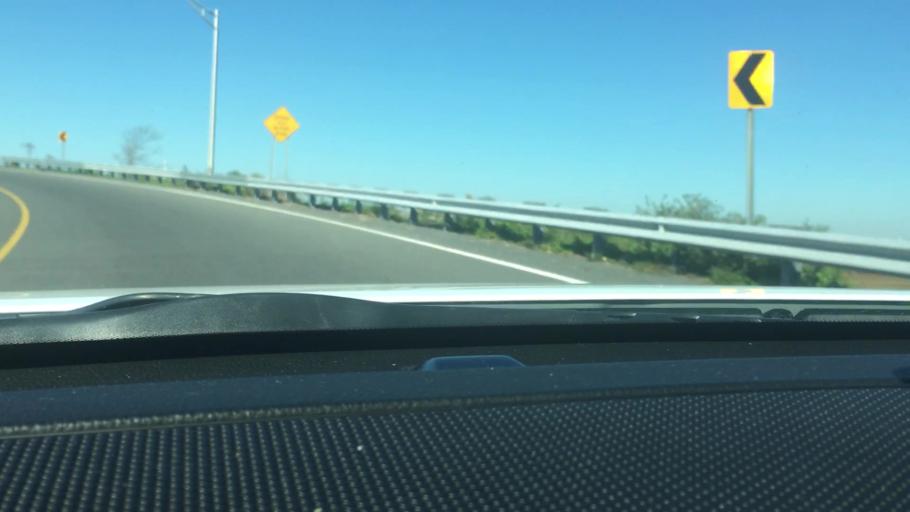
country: US
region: New Jersey
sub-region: Atlantic County
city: Pleasantville
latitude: 39.3956
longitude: -74.4916
